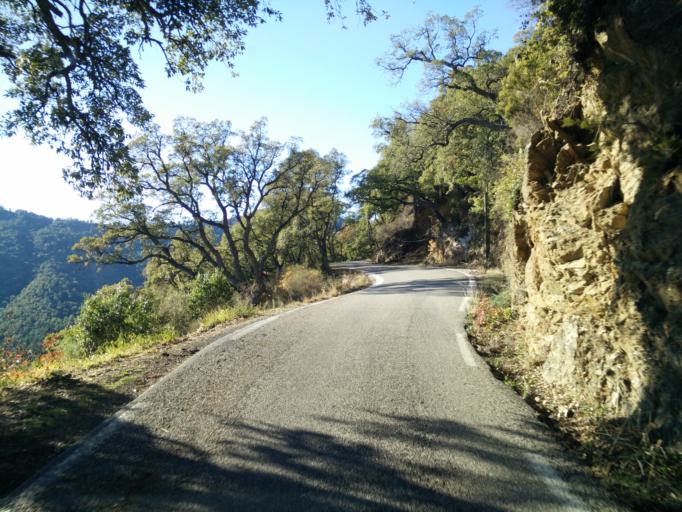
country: FR
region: Provence-Alpes-Cote d'Azur
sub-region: Departement du Var
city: La Garde-Freinet
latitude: 43.2581
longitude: 6.4417
